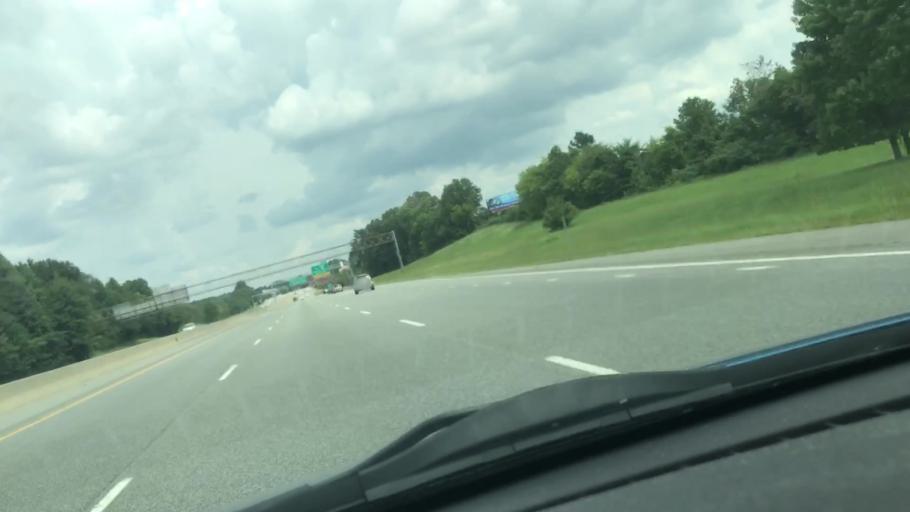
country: US
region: North Carolina
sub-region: Guilford County
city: Greensboro
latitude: 36.0291
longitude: -79.8230
